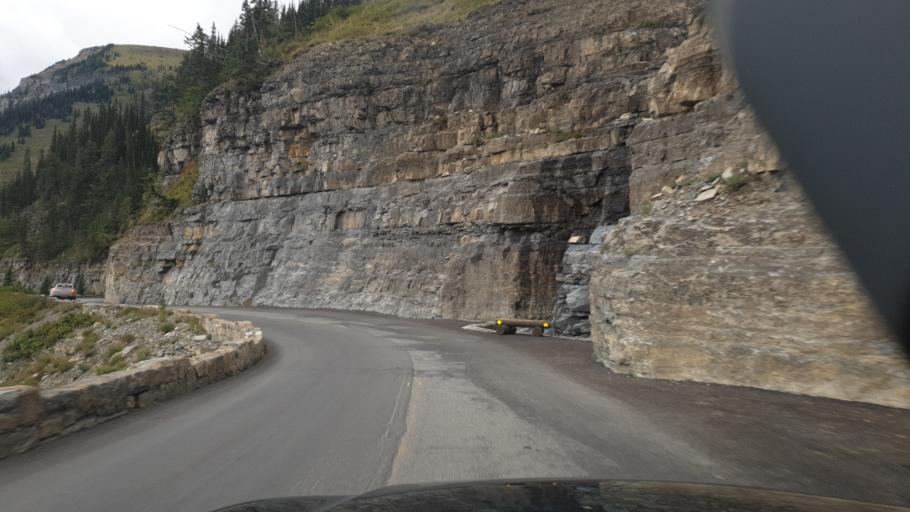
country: US
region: Montana
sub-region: Flathead County
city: Columbia Falls
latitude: 48.7190
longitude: -113.7215
